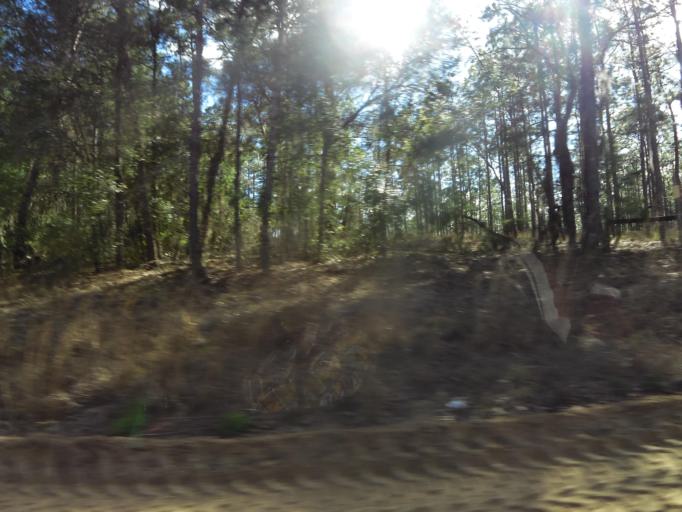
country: US
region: Florida
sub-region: Putnam County
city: Interlachen
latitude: 29.7852
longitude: -81.8678
